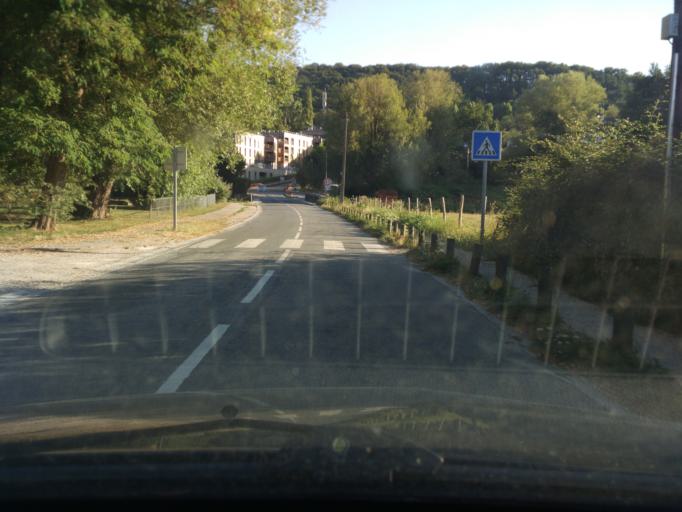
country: FR
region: Ile-de-France
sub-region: Departement des Yvelines
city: Saint-Remy-les-Chevreuse
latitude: 48.7034
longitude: 2.0556
